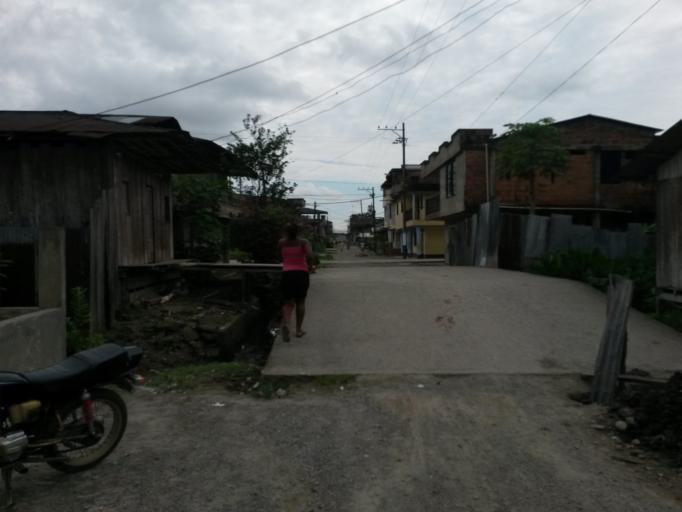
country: CO
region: Cauca
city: Guapi
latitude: 2.5715
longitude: -77.8866
